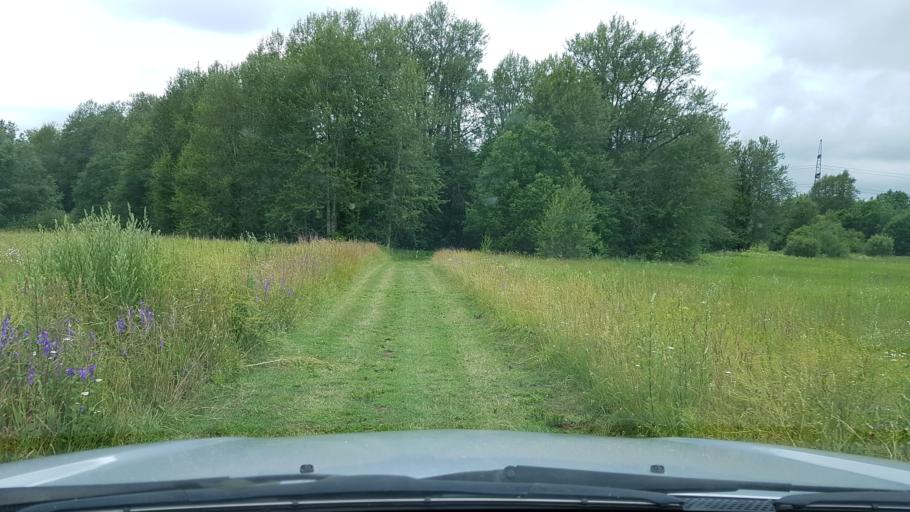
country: EE
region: Ida-Virumaa
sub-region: Narva-Joesuu linn
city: Narva-Joesuu
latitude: 59.3485
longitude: 28.0084
